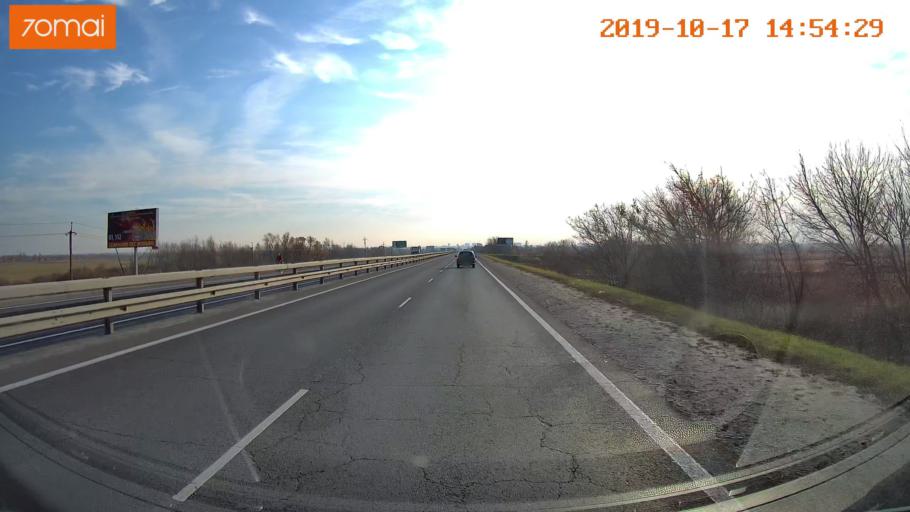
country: RU
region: Rjazan
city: Polyany
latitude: 54.6809
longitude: 39.8319
